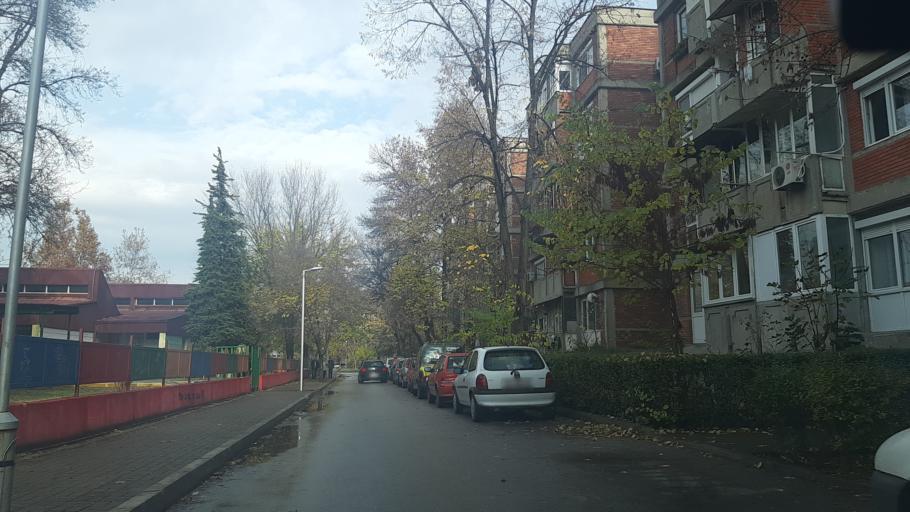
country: MK
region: Kisela Voda
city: Usje
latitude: 41.9858
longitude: 21.4586
